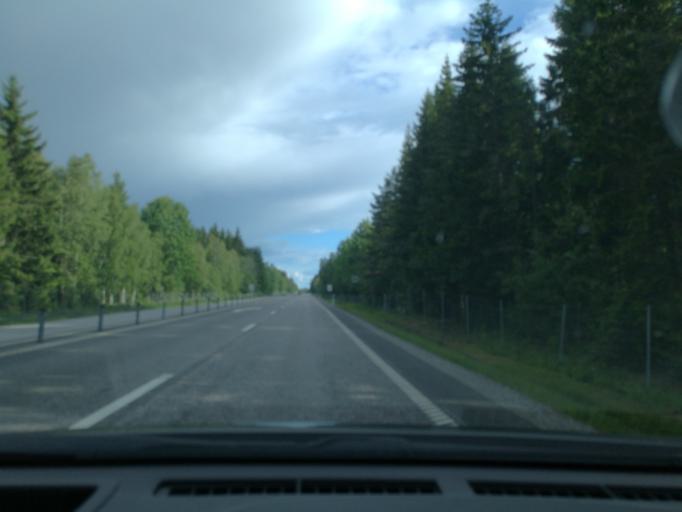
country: SE
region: Vaestmanland
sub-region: Surahammars Kommun
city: Ramnas
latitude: 59.7449
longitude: 16.2263
